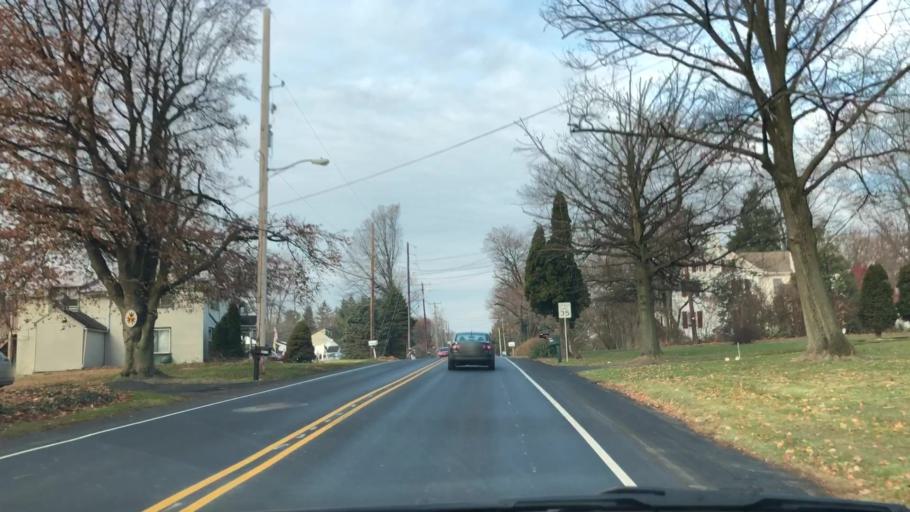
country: US
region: Pennsylvania
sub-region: Lancaster County
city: Landisville
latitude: 40.0562
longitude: -76.3889
